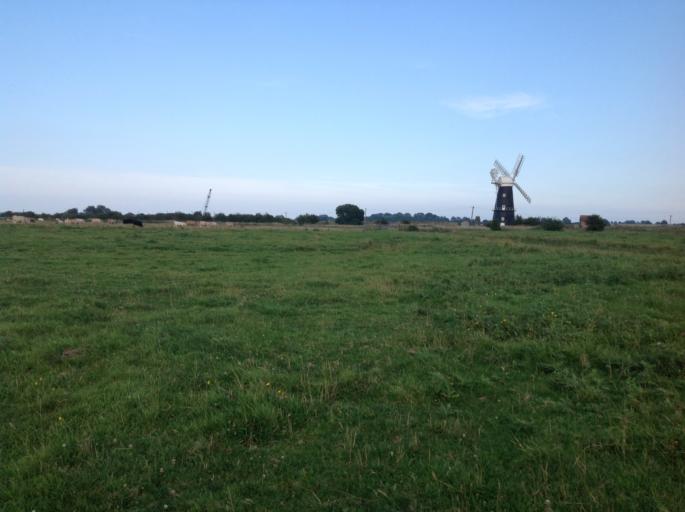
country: GB
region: England
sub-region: Norfolk
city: Gorleston-on-Sea
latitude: 52.5871
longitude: 1.6339
